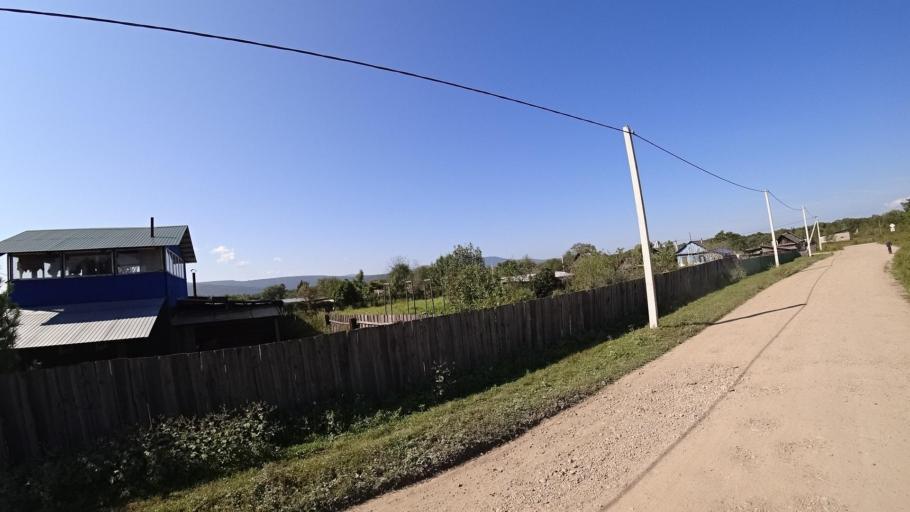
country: RU
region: Jewish Autonomous Oblast
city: Bira
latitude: 48.9996
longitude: 132.4522
